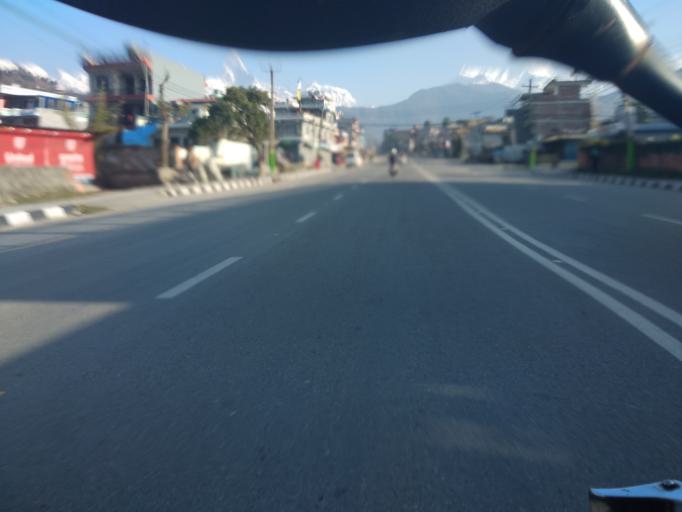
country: NP
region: Western Region
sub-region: Gandaki Zone
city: Pokhara
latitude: 28.2339
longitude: 83.9829
